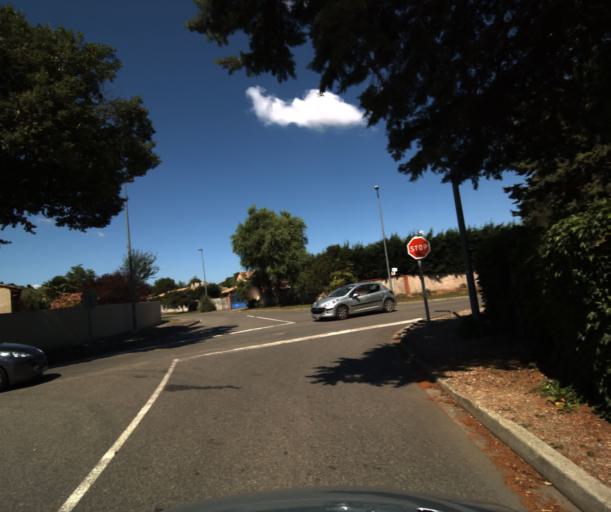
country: FR
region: Midi-Pyrenees
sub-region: Departement de la Haute-Garonne
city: Eaunes
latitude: 43.4270
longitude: 1.3480
